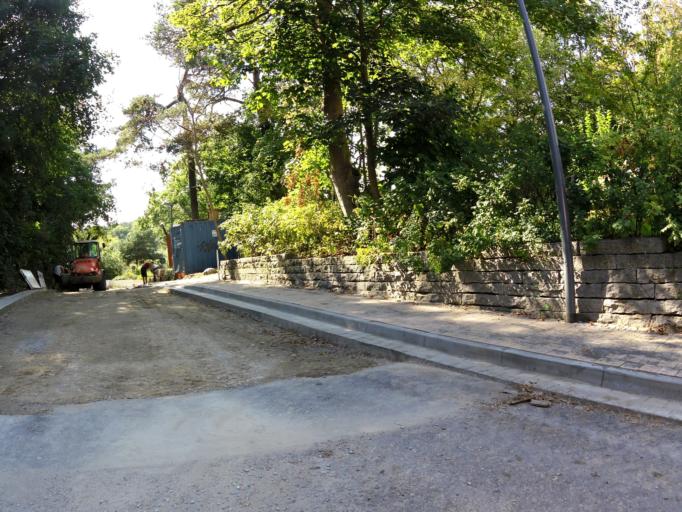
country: DE
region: Mecklenburg-Vorpommern
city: Seebad Heringsdorf
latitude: 53.9473
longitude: 14.1782
